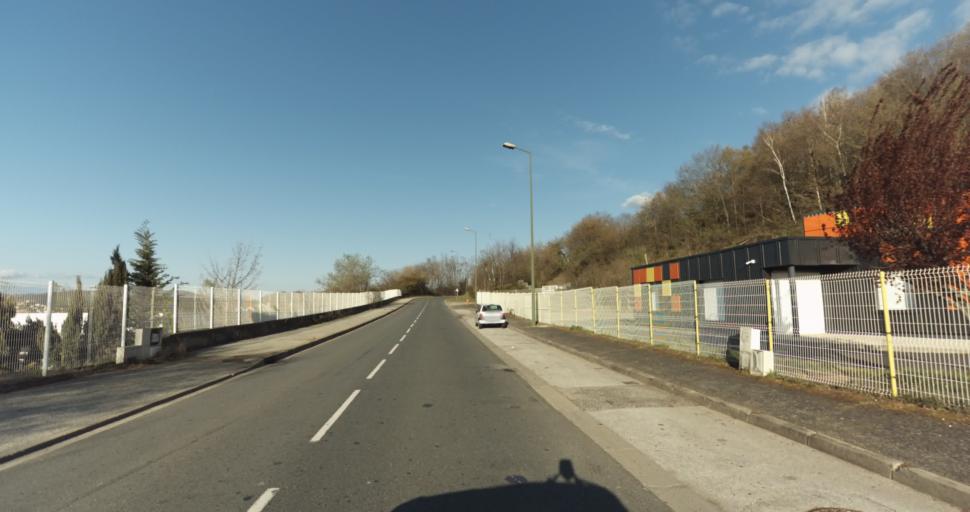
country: FR
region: Rhone-Alpes
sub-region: Departement de la Loire
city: La Talaudiere
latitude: 45.4680
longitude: 4.4353
